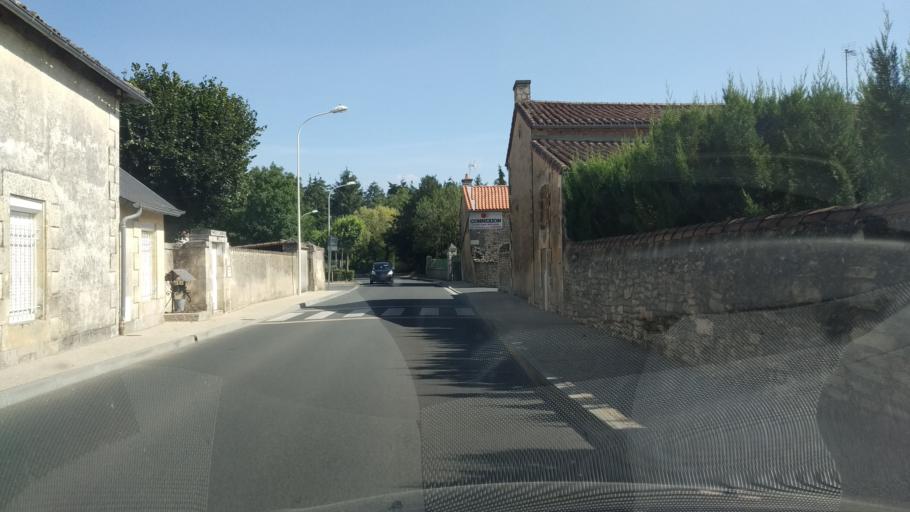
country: FR
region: Poitou-Charentes
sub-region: Departement de la Vienne
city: Cisse
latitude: 46.6445
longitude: 0.2314
